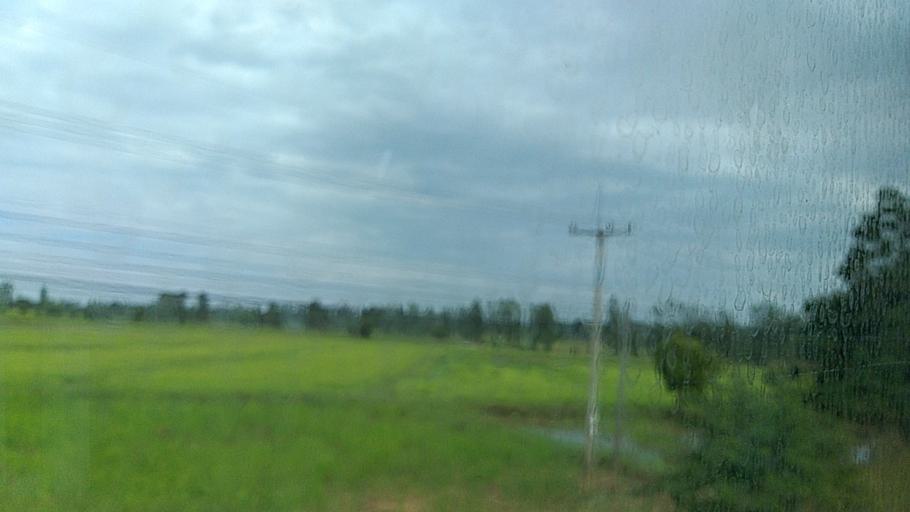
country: TH
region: Maha Sarakham
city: Chiang Yuen
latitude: 16.3356
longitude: 103.1809
